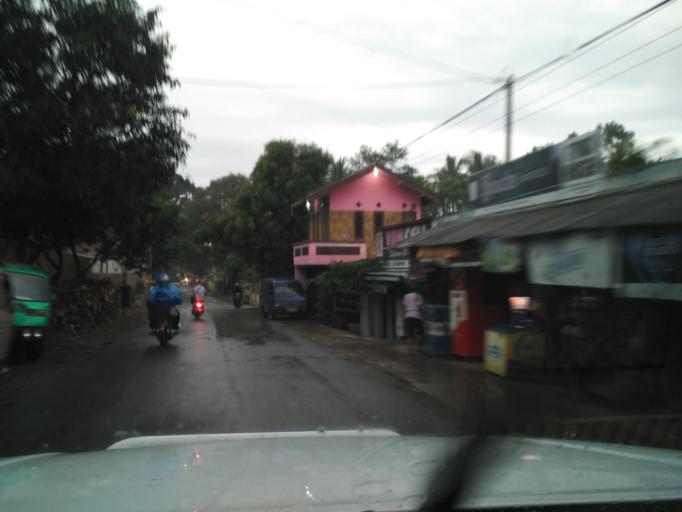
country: ID
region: West Java
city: Ciranjang-hilir
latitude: -6.7500
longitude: 107.1957
